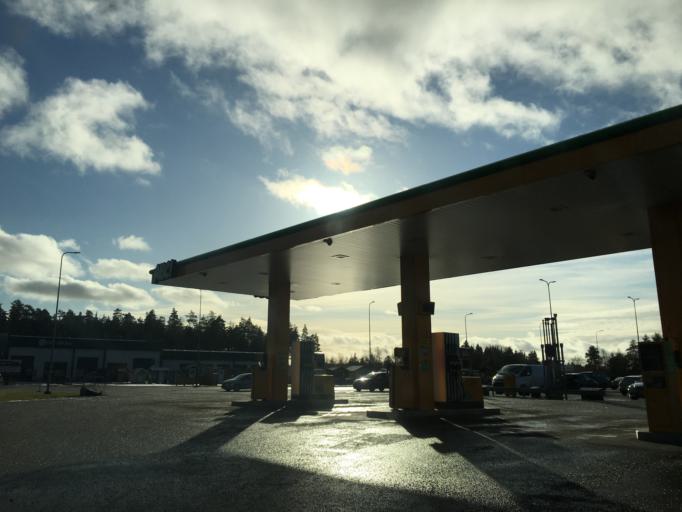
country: FI
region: Varsinais-Suomi
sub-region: Turku
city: Raisio
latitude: 60.5056
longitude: 22.1603
